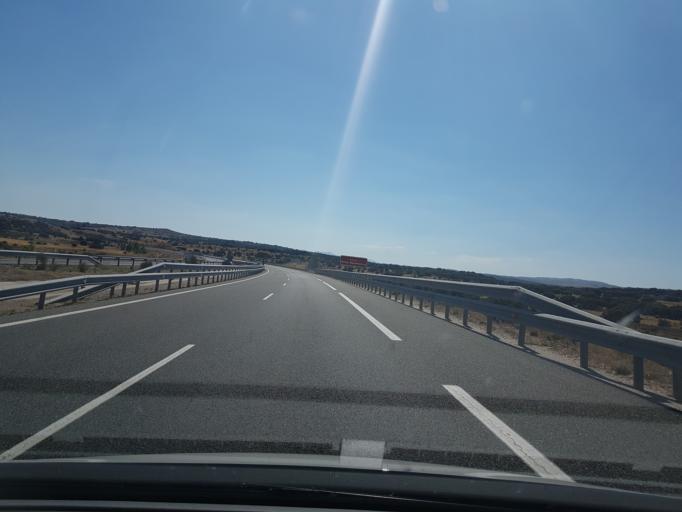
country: ES
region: Castille and Leon
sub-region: Provincia de Avila
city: Cardenosa
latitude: 40.7492
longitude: -4.7593
